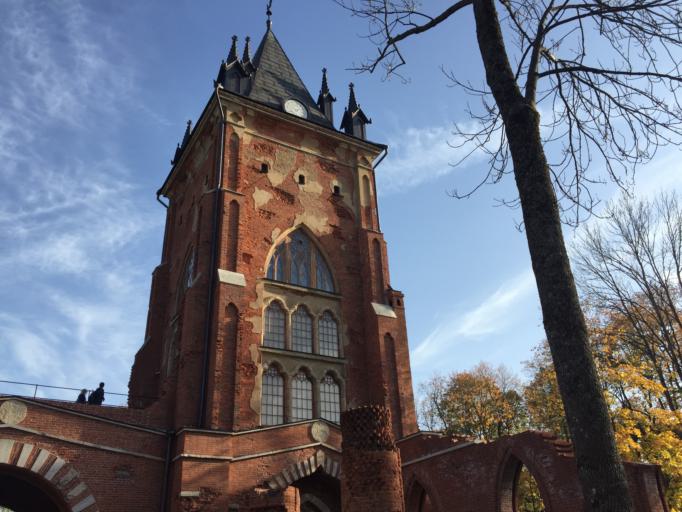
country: RU
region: St.-Petersburg
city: Pushkin
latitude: 59.7155
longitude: 30.3796
